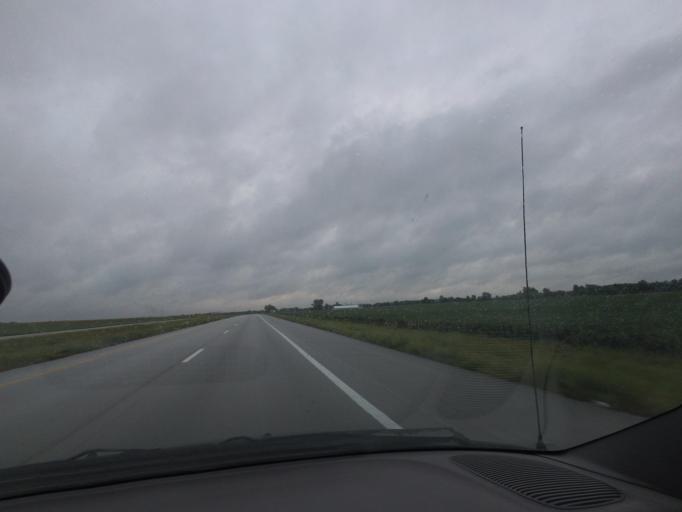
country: US
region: Missouri
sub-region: Marion County
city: Monroe City
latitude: 39.6644
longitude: -91.6866
